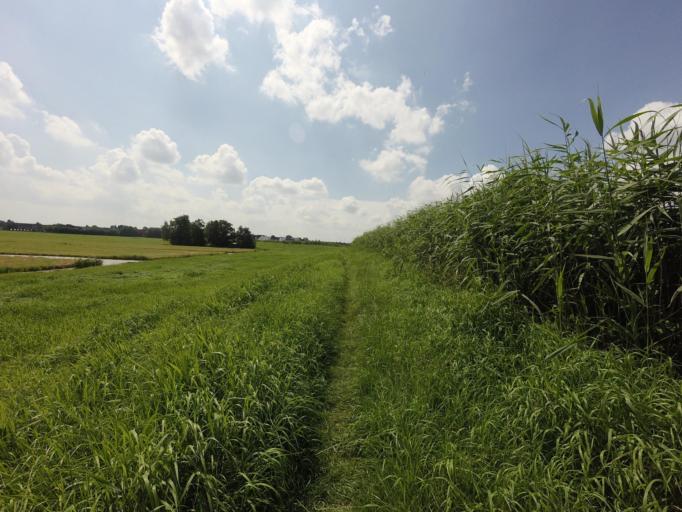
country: NL
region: South Holland
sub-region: Gemeente Vlist
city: Haastrecht
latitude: 52.0498
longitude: 4.7995
